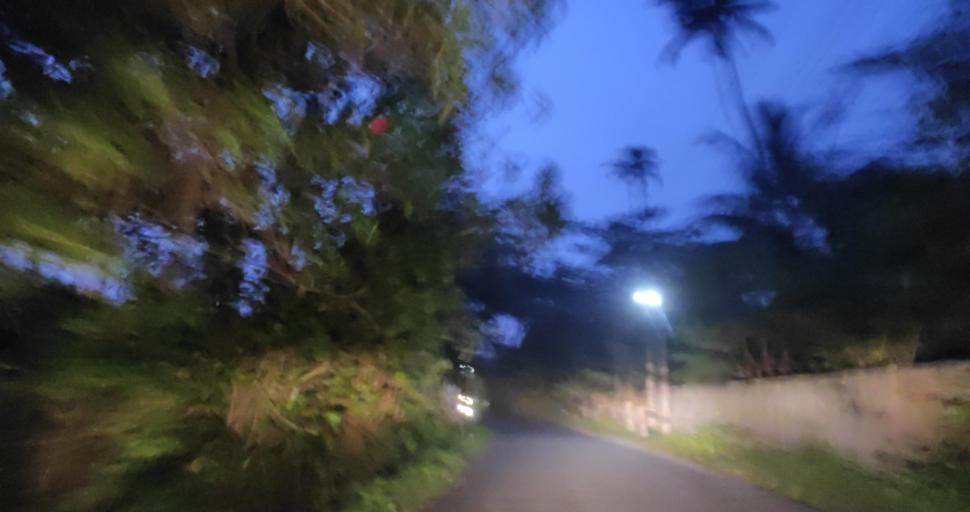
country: IN
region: Kerala
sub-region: Alappuzha
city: Vayalar
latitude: 9.7424
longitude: 76.2855
